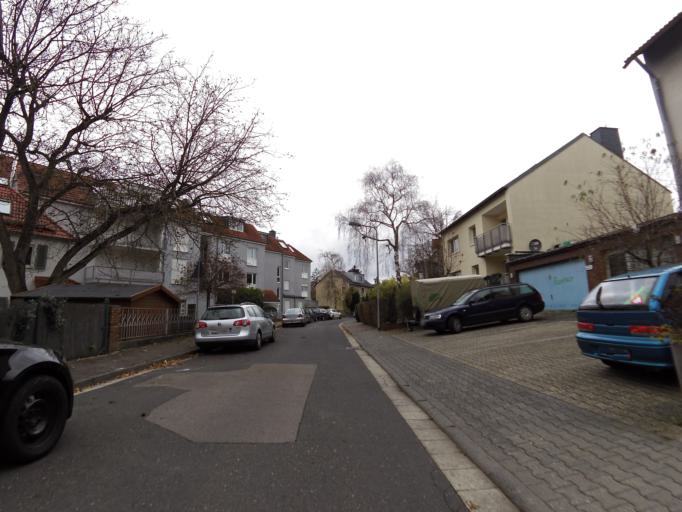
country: DE
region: Hesse
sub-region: Regierungsbezirk Darmstadt
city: Bad Vilbel
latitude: 50.1458
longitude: 8.7508
